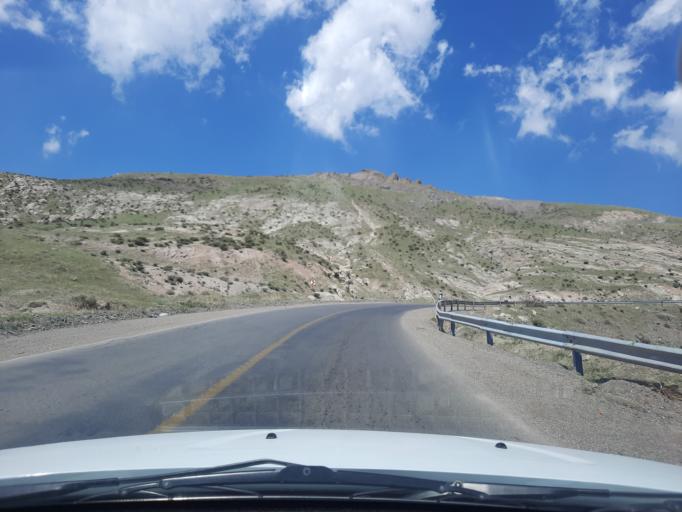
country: IR
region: Qazvin
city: Qazvin
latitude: 36.3675
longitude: 50.2007
